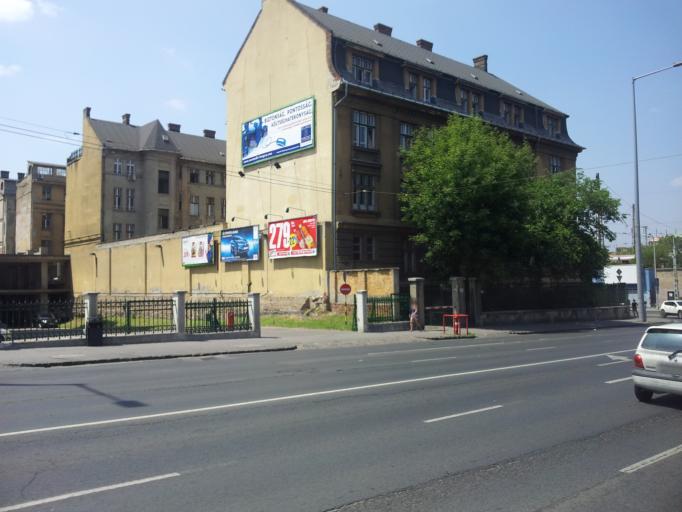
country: HU
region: Budapest
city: Budapest XIII. keruelet
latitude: 47.5169
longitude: 19.0740
